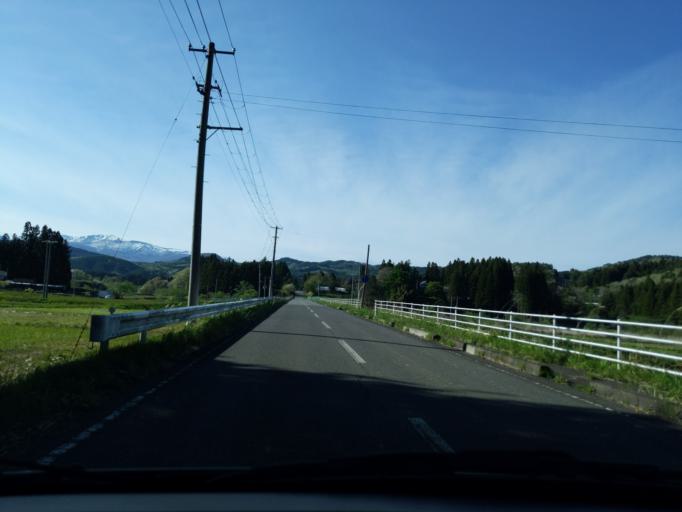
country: JP
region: Iwate
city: Ichinoseki
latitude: 38.8642
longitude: 140.9055
